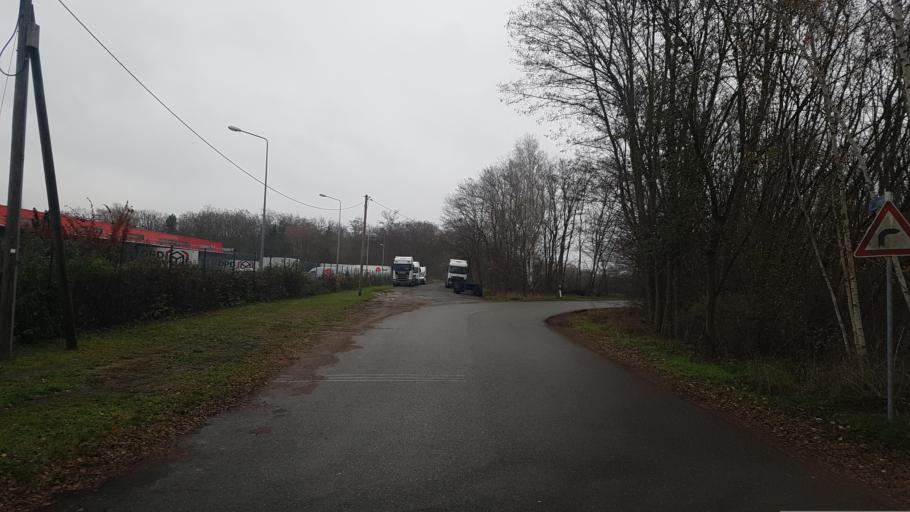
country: DE
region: Brandenburg
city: Lubbenau
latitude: 51.8381
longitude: 13.9024
